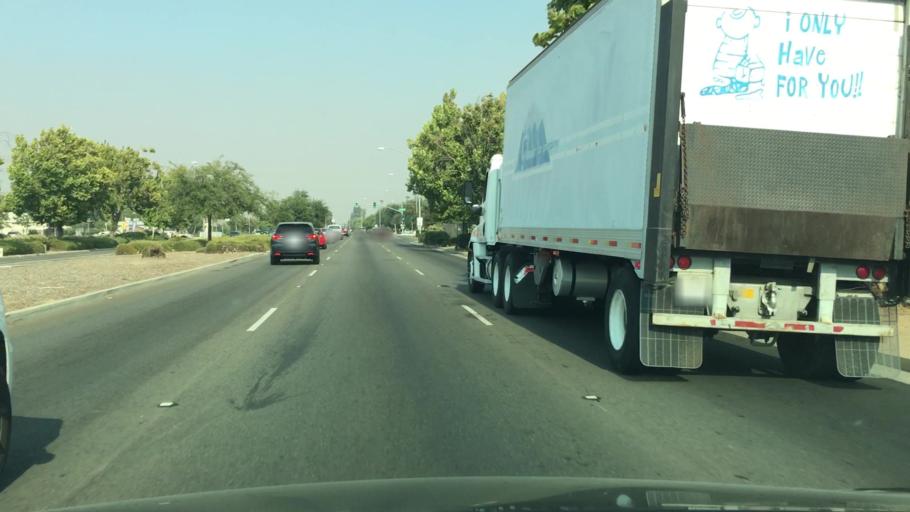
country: US
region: California
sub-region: Fresno County
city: Fresno
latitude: 36.8370
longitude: -119.8013
